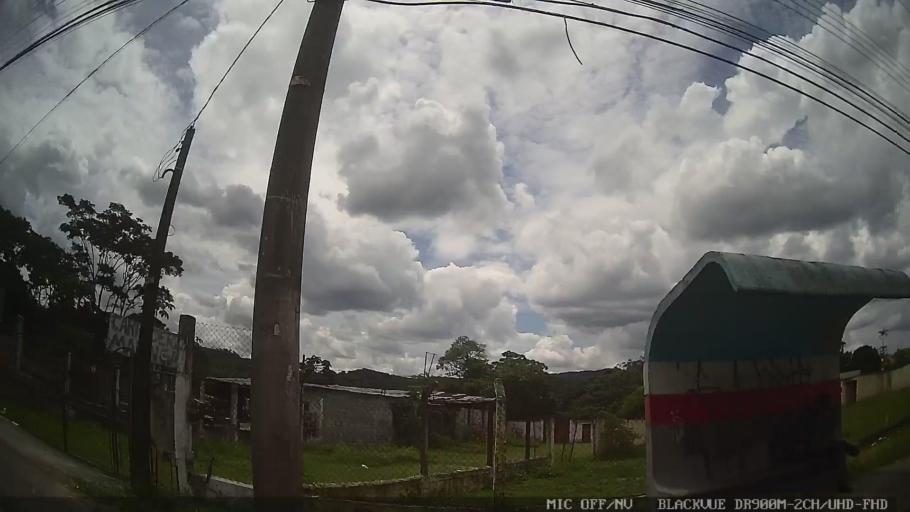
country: BR
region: Sao Paulo
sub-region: Ribeirao Pires
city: Ribeirao Pires
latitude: -23.6633
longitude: -46.3397
